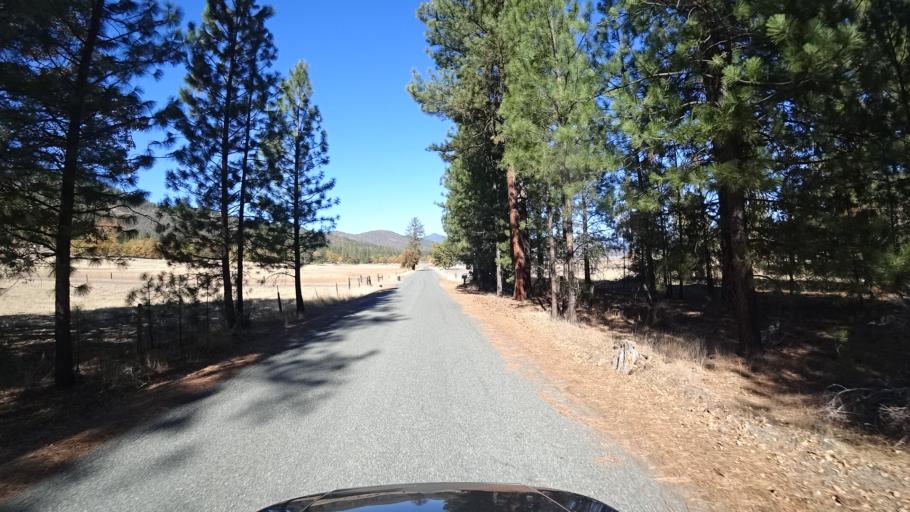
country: US
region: California
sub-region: Siskiyou County
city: Yreka
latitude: 41.5880
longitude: -122.9114
